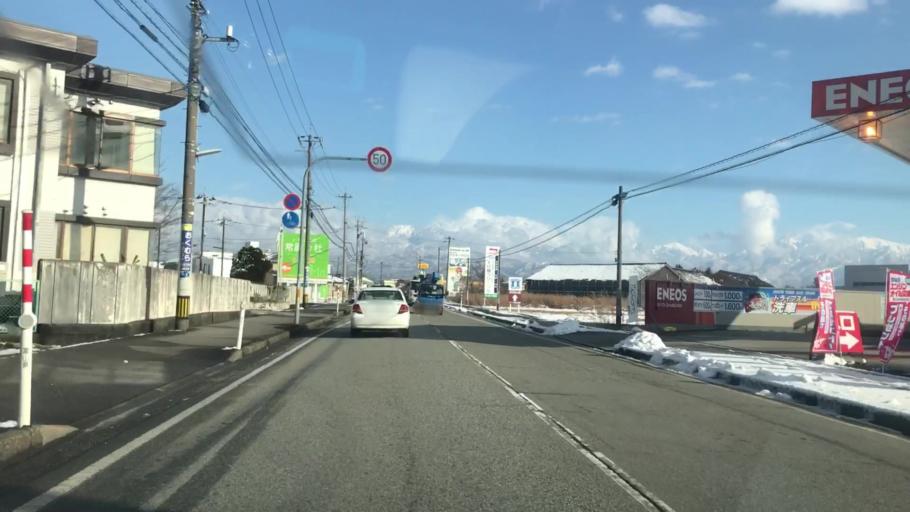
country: JP
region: Toyama
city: Toyama-shi
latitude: 36.6723
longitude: 137.2715
